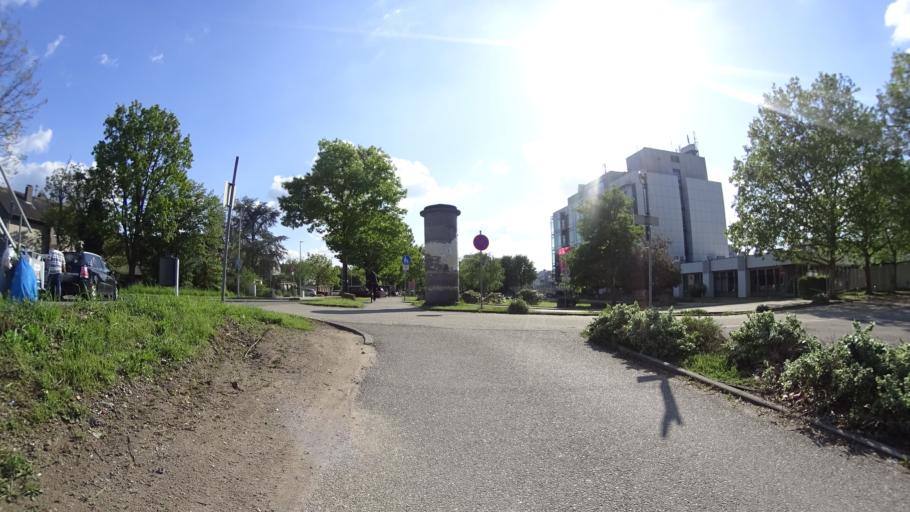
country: DE
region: Baden-Wuerttemberg
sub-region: Karlsruhe Region
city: Karlsruhe
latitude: 49.0392
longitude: 8.3707
